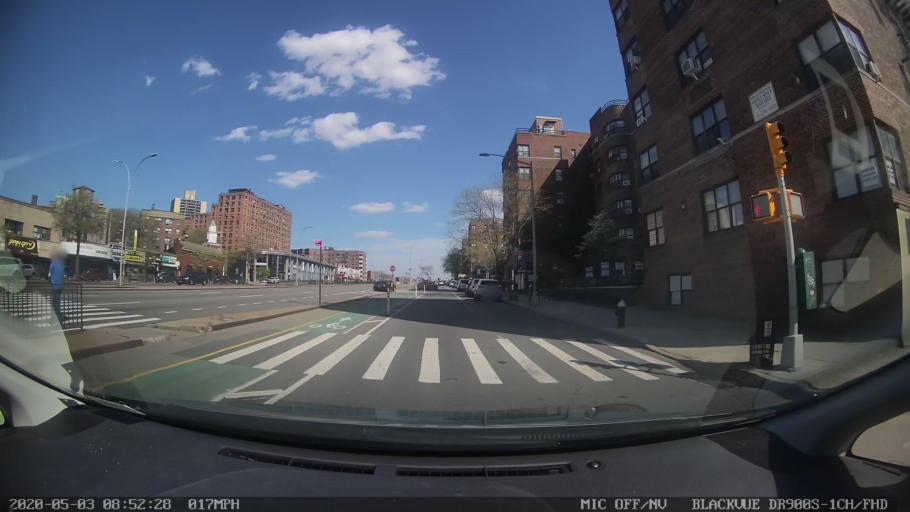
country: US
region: New York
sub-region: Queens County
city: Borough of Queens
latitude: 40.7313
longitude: -73.8573
